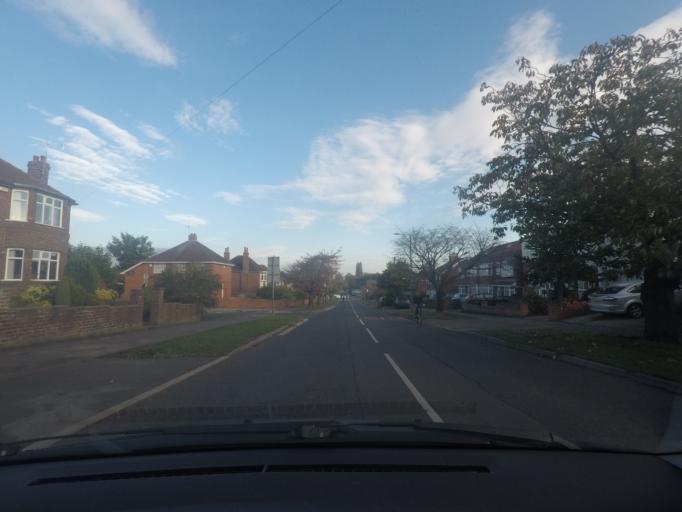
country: GB
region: England
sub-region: City of York
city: Heslington
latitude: 53.9525
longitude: -1.0593
